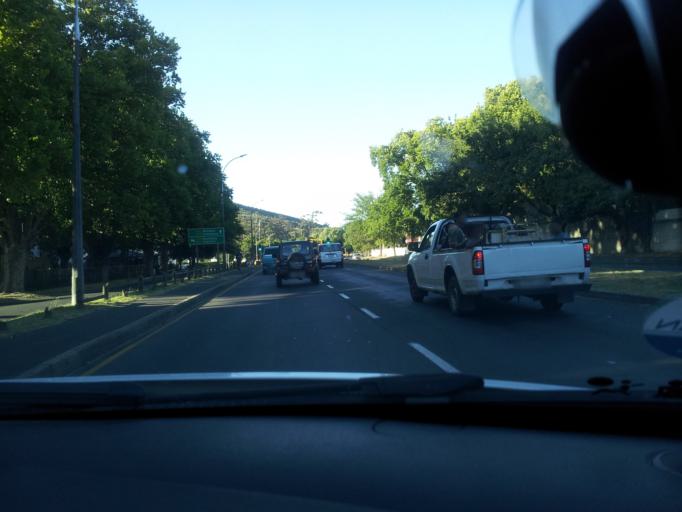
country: ZA
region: Western Cape
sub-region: Cape Winelands District Municipality
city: Stellenbosch
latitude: -33.9391
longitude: 18.8518
